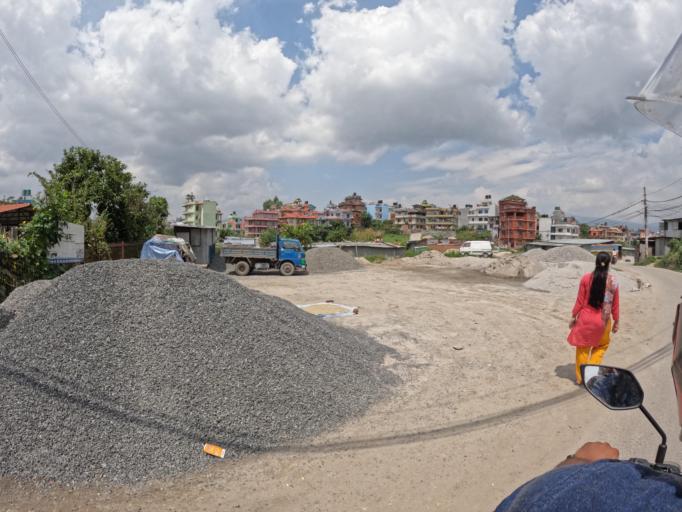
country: NP
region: Central Region
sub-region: Bagmati Zone
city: Kathmandu
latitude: 27.6772
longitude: 85.3658
